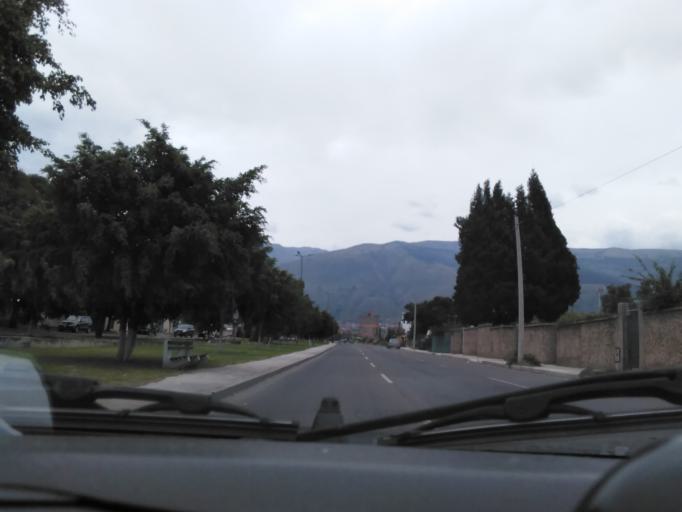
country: BO
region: Cochabamba
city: Cochabamba
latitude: -17.3700
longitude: -66.1796
